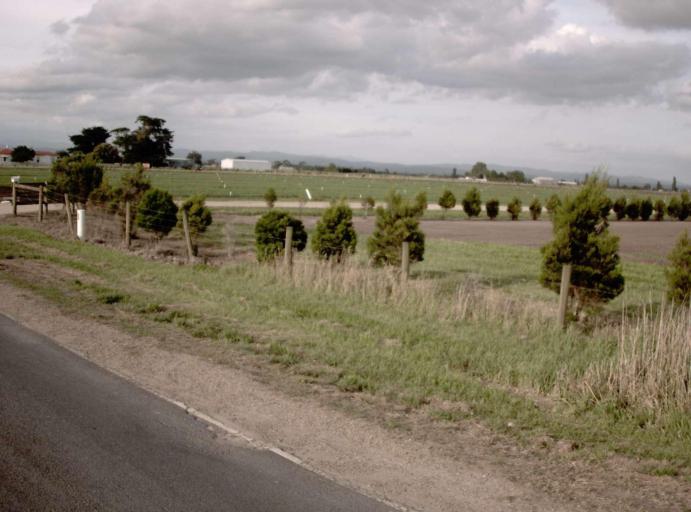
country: AU
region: Victoria
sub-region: Wellington
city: Sale
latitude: -37.9043
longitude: 146.9942
